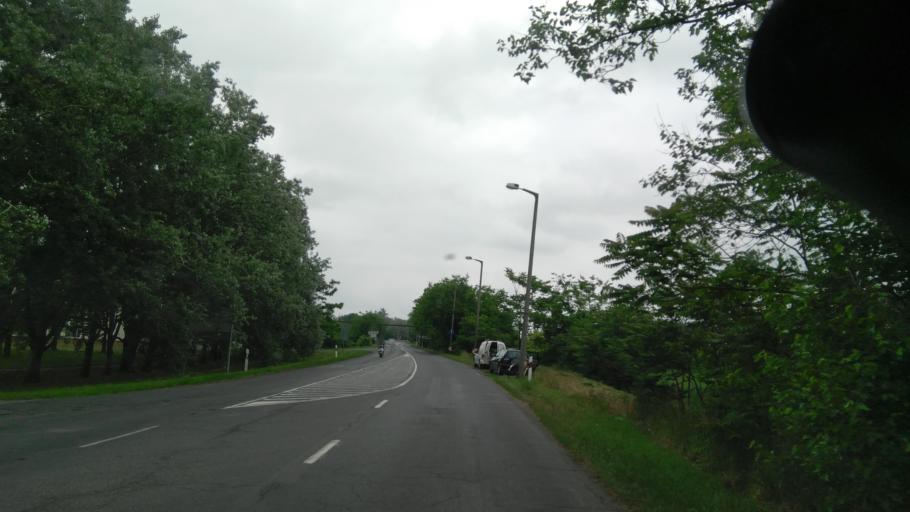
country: HU
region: Bekes
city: Bekescsaba
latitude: 46.6920
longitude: 21.0966
